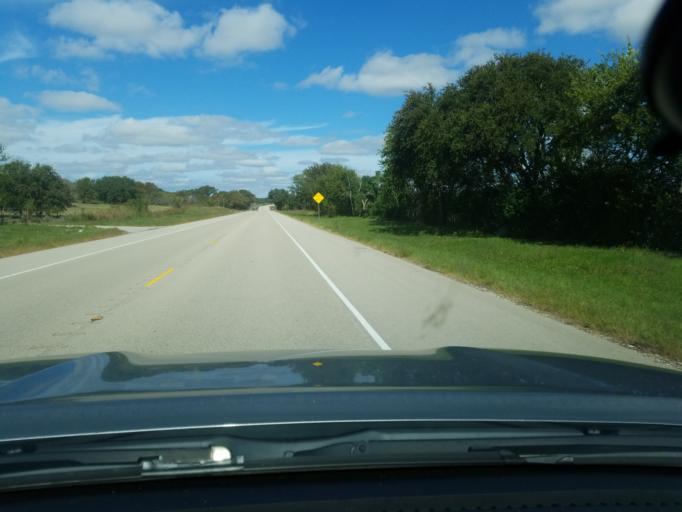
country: US
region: Texas
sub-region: Hamilton County
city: Hamilton
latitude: 31.6053
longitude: -98.1582
